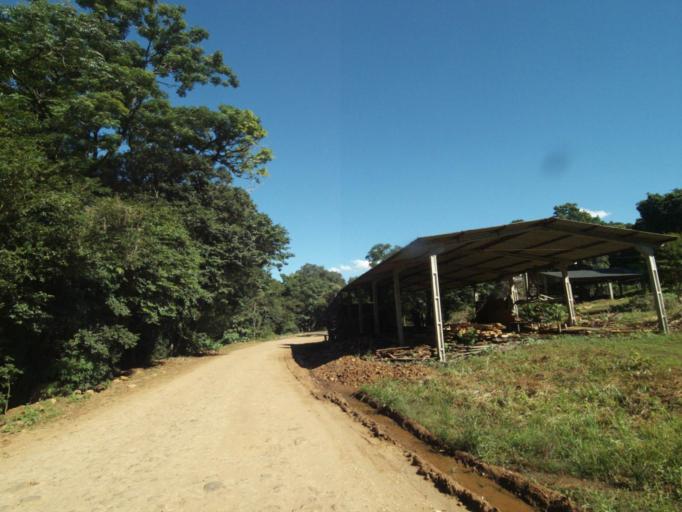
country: BR
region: Parana
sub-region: Ampere
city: Ampere
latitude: -26.1709
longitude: -53.3646
